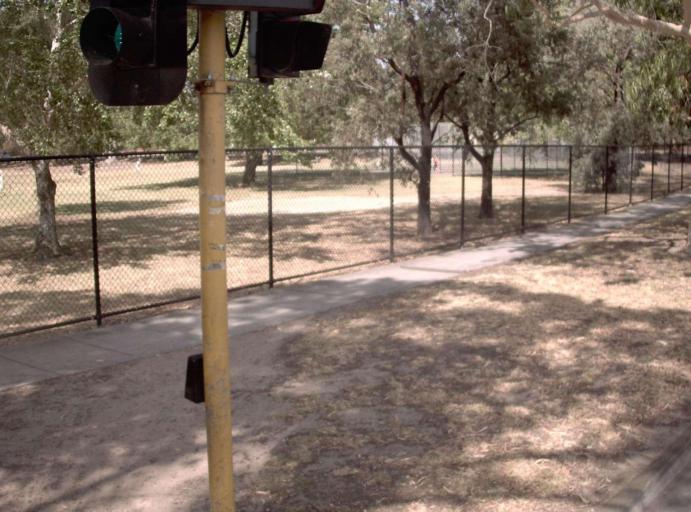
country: AU
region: Victoria
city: Carnegie
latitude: -37.8790
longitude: 145.0688
